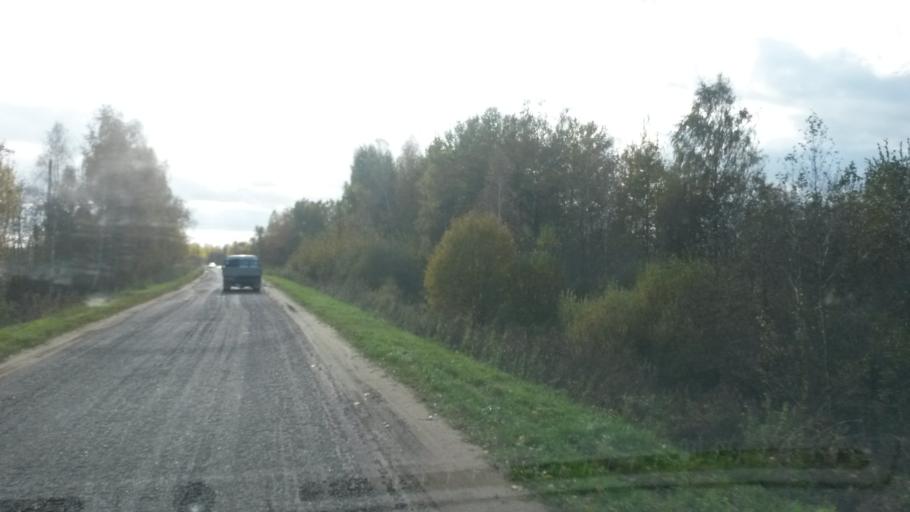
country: RU
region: Jaroslavl
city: Tunoshna
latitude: 57.5332
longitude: 40.0164
